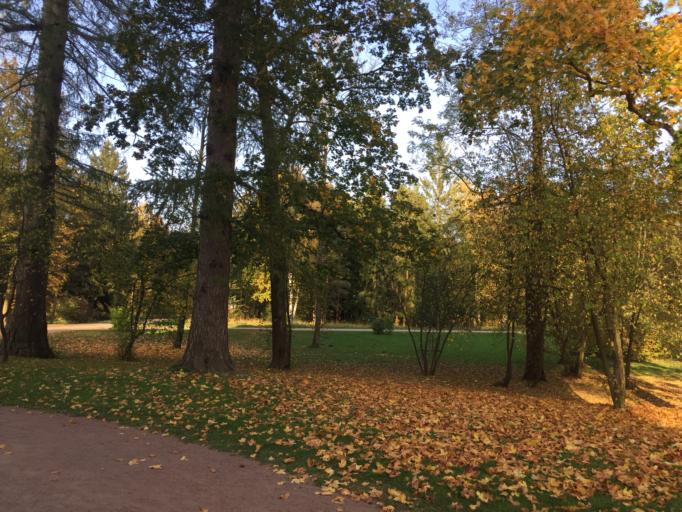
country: RU
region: St.-Petersburg
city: Pushkin
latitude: 59.7217
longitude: 30.3778
